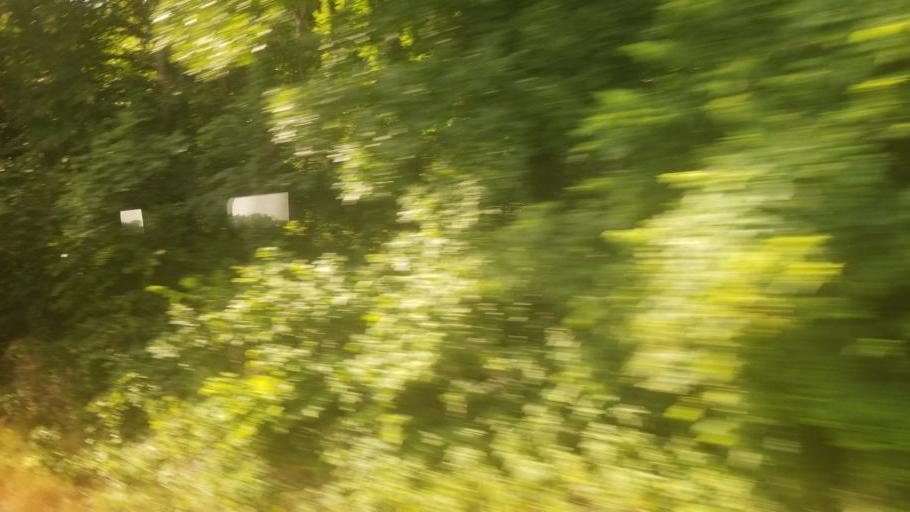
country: US
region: Kansas
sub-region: Wyandotte County
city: Edwardsville
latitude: 39.0461
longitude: -94.8226
